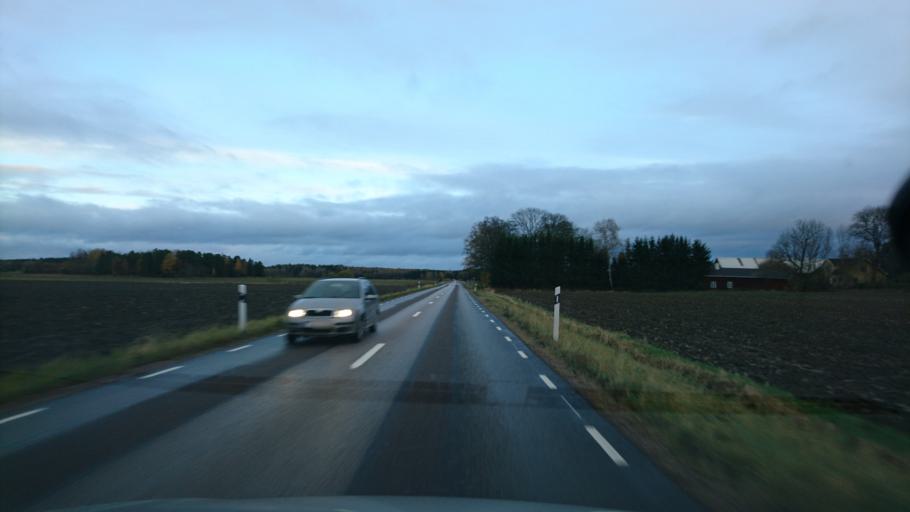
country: SE
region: Uppsala
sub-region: Uppsala Kommun
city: Vattholma
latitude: 59.9506
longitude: 17.9095
